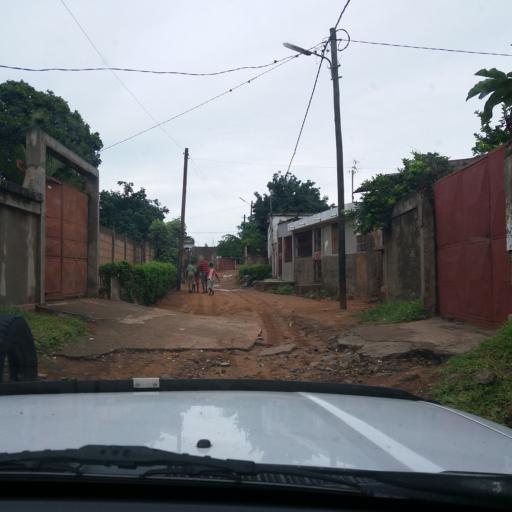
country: MZ
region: Maputo City
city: Maputo
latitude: -25.9123
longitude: 32.5915
